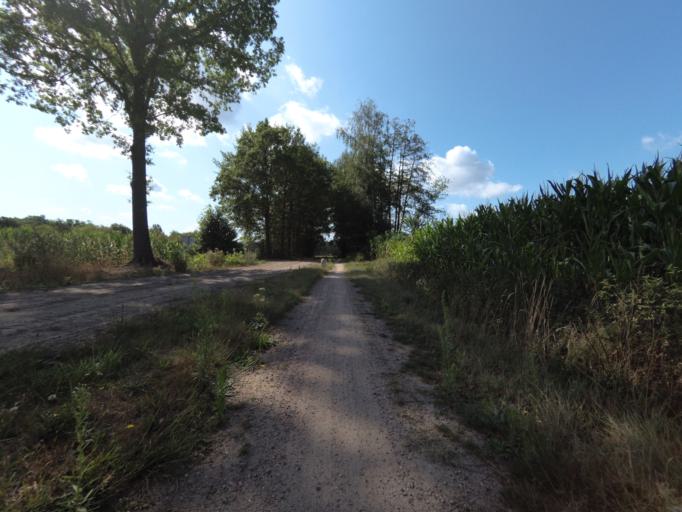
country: NL
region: Overijssel
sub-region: Gemeente Oldenzaal
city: Oldenzaal
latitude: 52.2828
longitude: 6.8795
